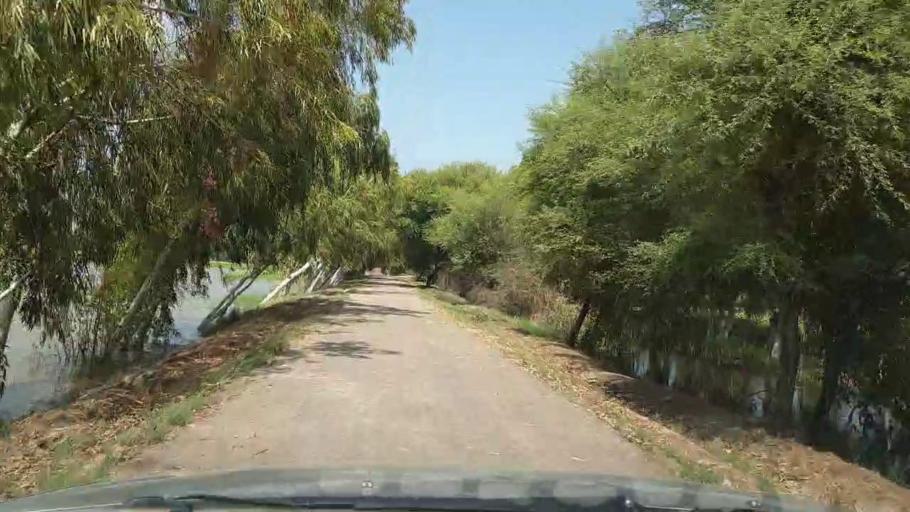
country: PK
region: Sindh
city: Rajo Khanani
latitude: 25.0370
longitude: 68.9364
